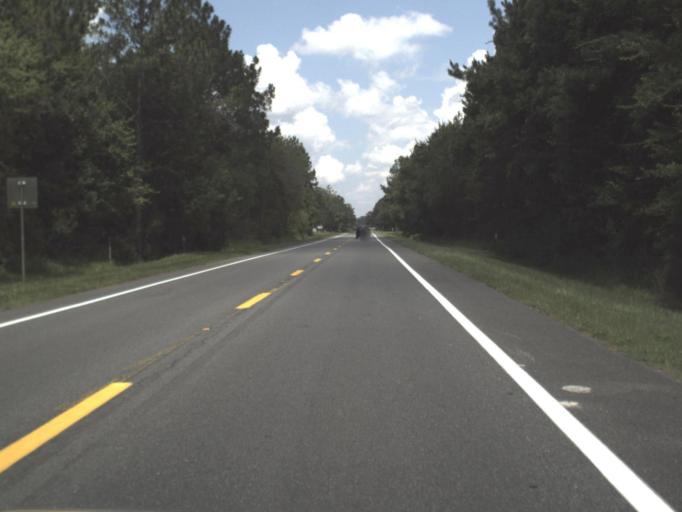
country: US
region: Florida
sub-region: Union County
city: Lake Butler
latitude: 30.0054
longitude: -82.3667
